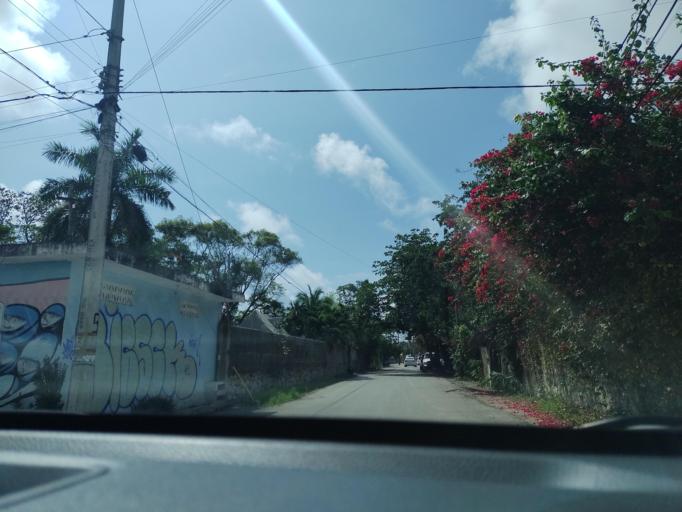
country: MX
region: Quintana Roo
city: Tulum
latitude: 20.2117
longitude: -87.4706
